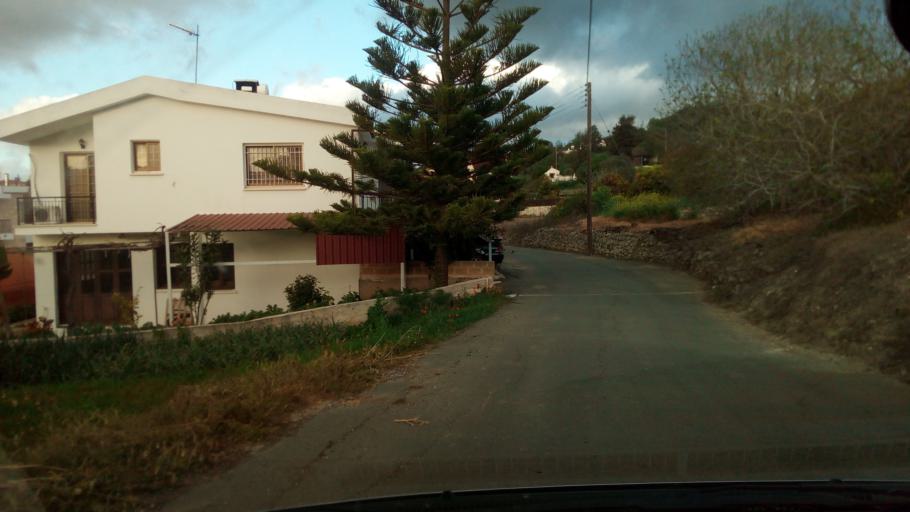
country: CY
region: Pafos
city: Polis
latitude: 34.9972
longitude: 32.5124
